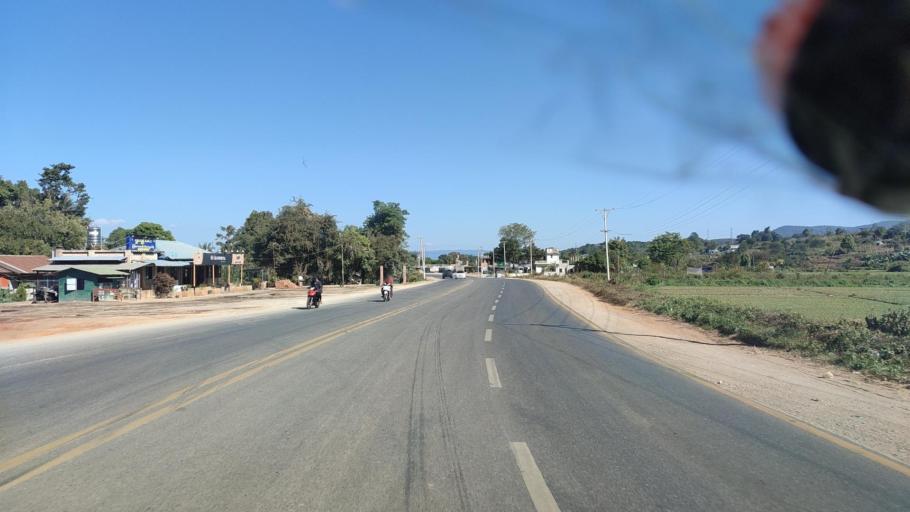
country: MM
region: Mandalay
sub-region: Pyin Oo Lwin District
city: Pyin Oo Lwin
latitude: 22.0808
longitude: 96.5784
